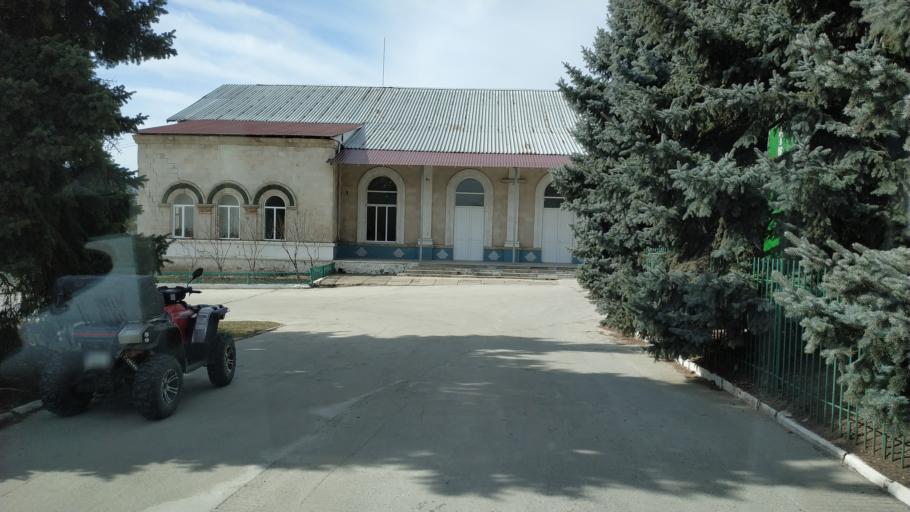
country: MD
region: Straseni
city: Straseni
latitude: 47.0946
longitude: 28.6648
